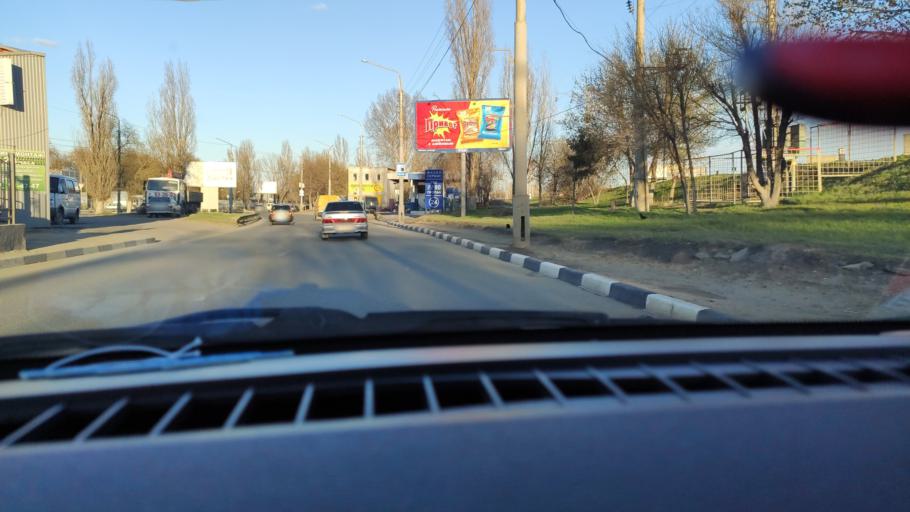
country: RU
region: Saratov
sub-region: Saratovskiy Rayon
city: Saratov
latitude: 51.5801
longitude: 45.9803
